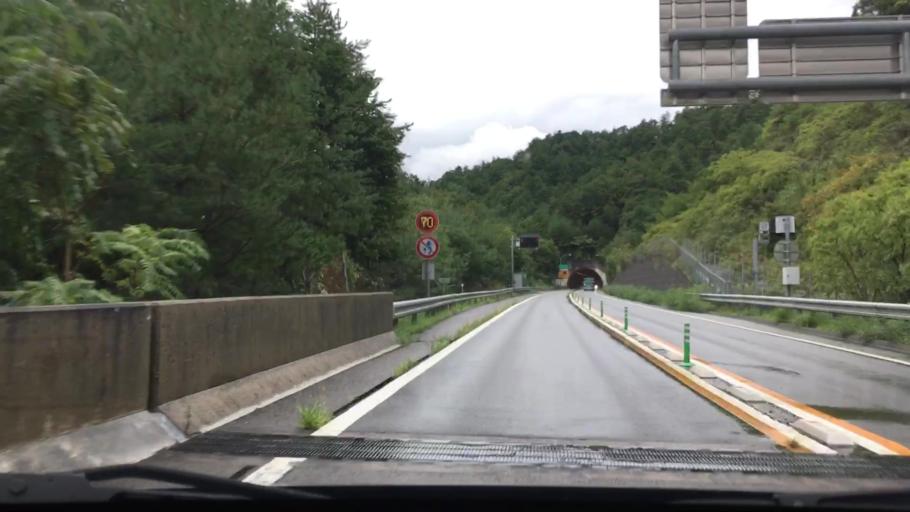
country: JP
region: Hyogo
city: Toyooka
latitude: 35.2769
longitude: 134.8158
